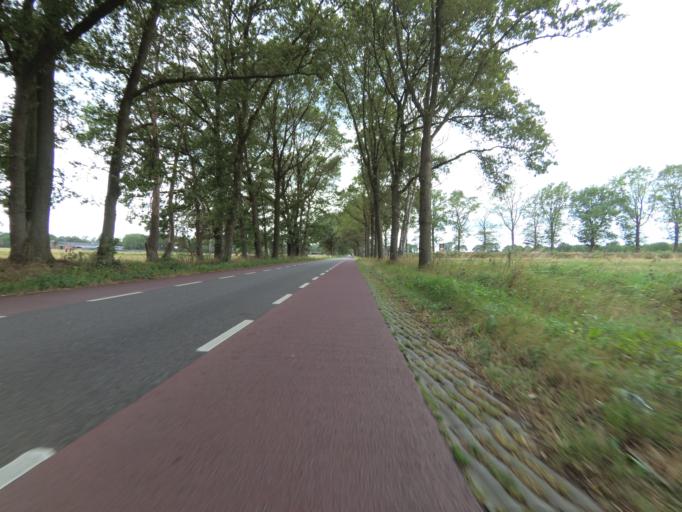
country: NL
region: Overijssel
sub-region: Gemeente Enschede
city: Enschede
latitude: 52.2633
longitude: 6.9080
